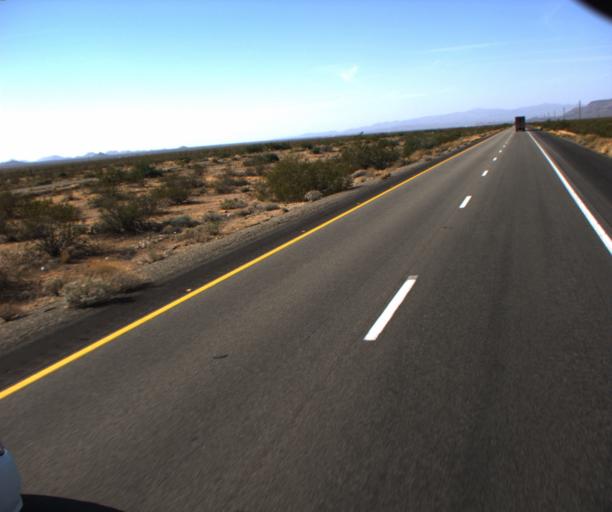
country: US
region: Arizona
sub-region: Mohave County
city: Kingman
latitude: 34.9549
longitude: -114.1455
